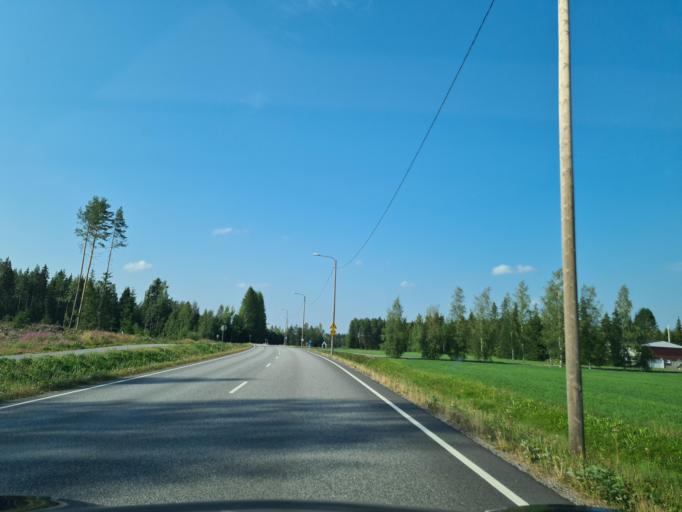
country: FI
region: Satakunta
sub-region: Pohjois-Satakunta
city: Karvia
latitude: 62.0868
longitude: 22.5271
